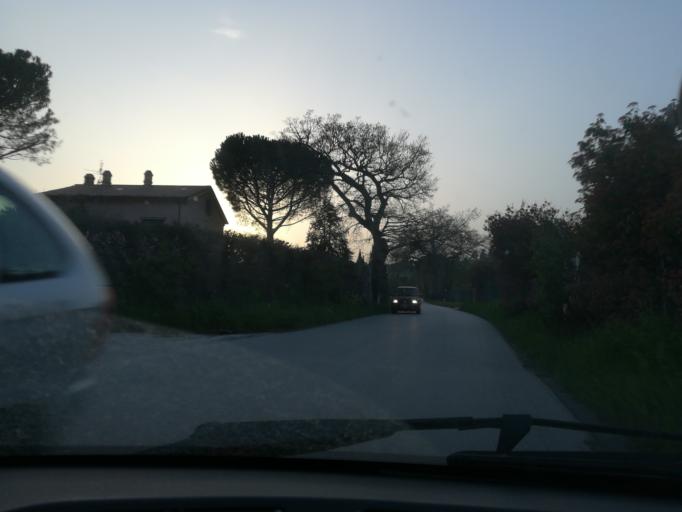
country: IT
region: The Marches
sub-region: Provincia di Macerata
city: Macerata
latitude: 43.2756
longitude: 13.4549
